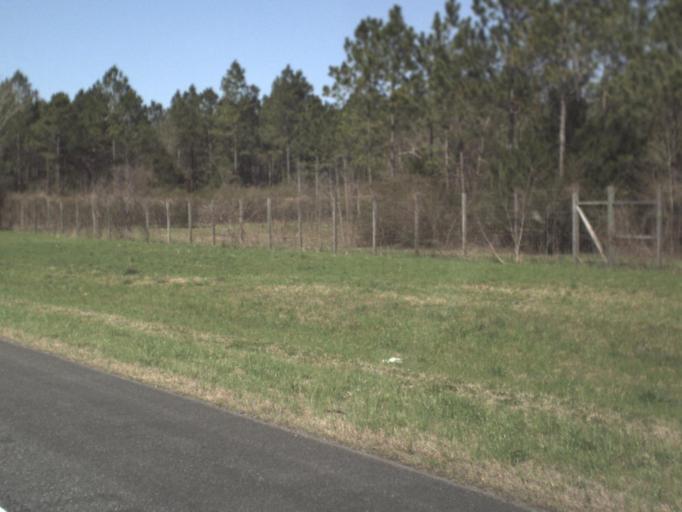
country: US
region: Florida
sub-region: Jackson County
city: Marianna
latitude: 30.7571
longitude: -85.3437
